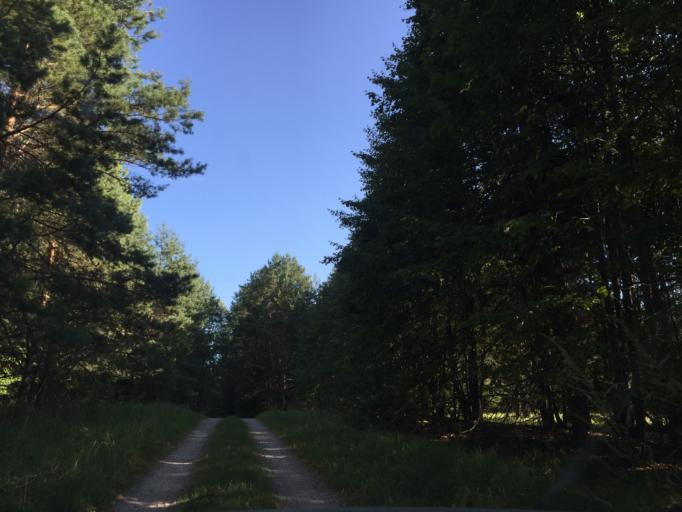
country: LT
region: Panevezys
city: Rokiskis
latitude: 55.8236
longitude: 25.8965
